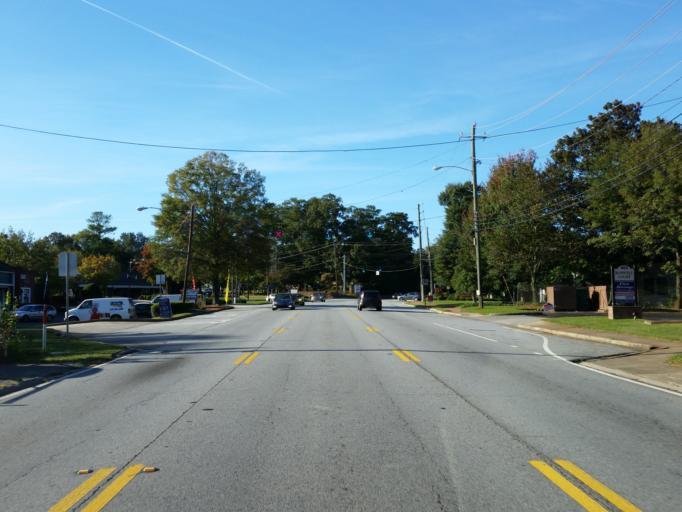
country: US
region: Georgia
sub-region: Fulton County
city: Roswell
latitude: 34.0108
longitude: -84.3620
